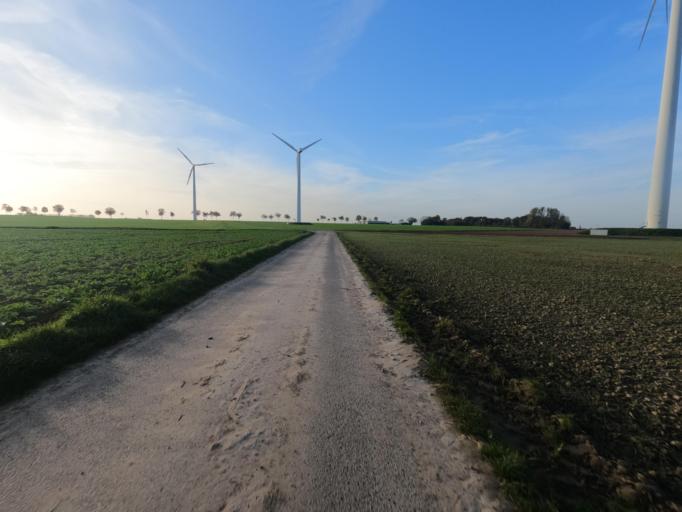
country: DE
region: North Rhine-Westphalia
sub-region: Regierungsbezirk Koln
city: Titz
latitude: 51.0470
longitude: 6.3777
